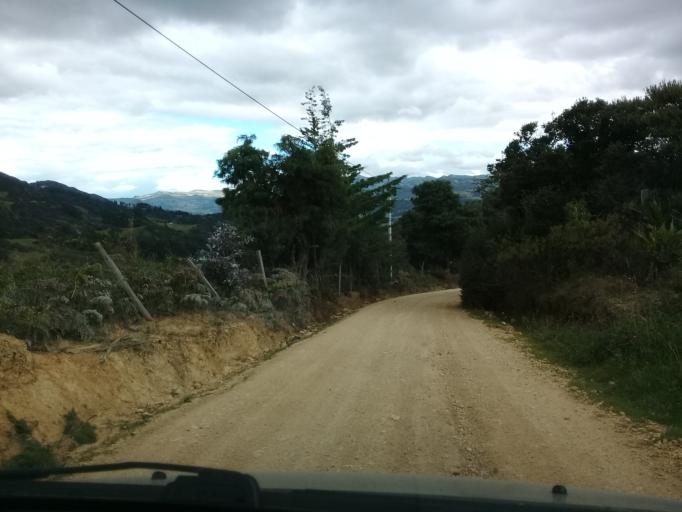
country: CO
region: Cundinamarca
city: Lenguazaque
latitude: 5.2859
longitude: -73.7378
